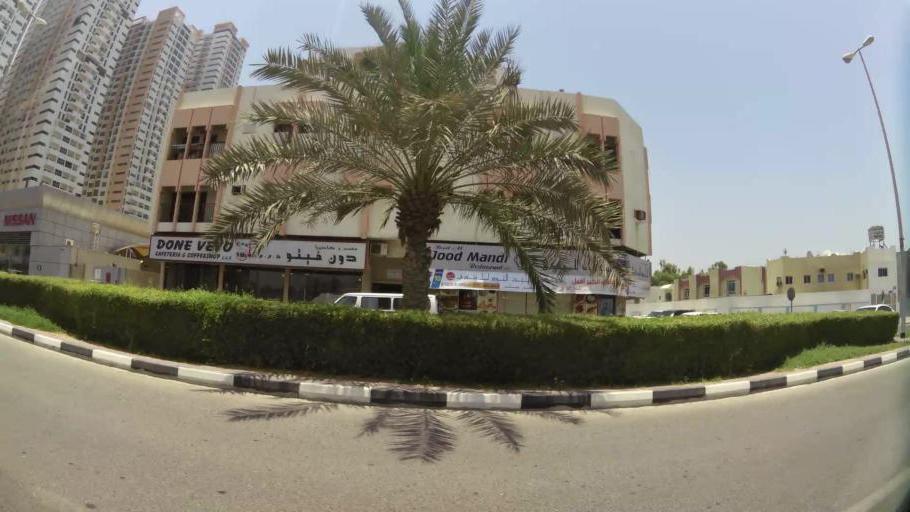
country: AE
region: Ajman
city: Ajman
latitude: 25.3974
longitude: 55.4302
